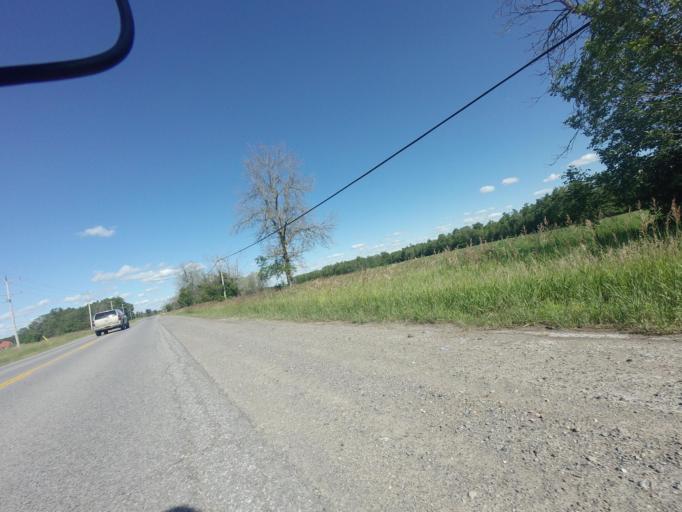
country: CA
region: Ontario
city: Arnprior
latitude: 45.4114
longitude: -76.4409
